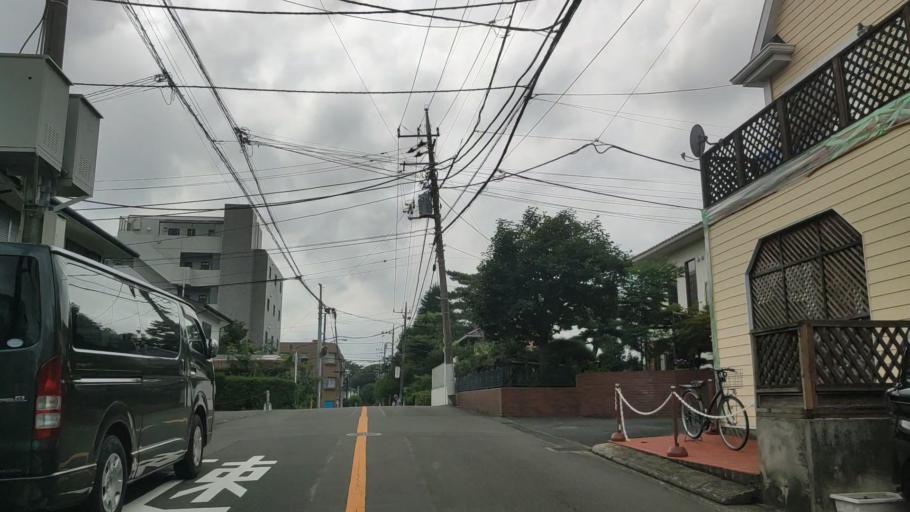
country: JP
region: Kanagawa
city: Minami-rinkan
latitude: 35.5086
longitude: 139.4410
